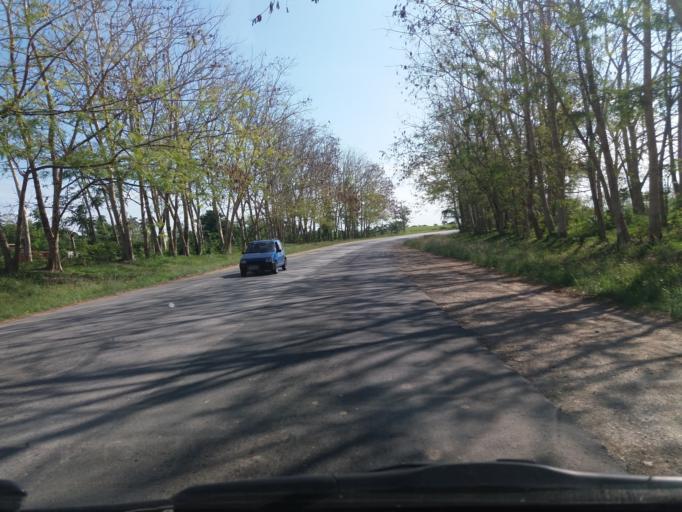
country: CU
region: Cienfuegos
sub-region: Municipio de Cienfuegos
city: Cienfuegos
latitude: 22.1647
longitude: -80.3997
